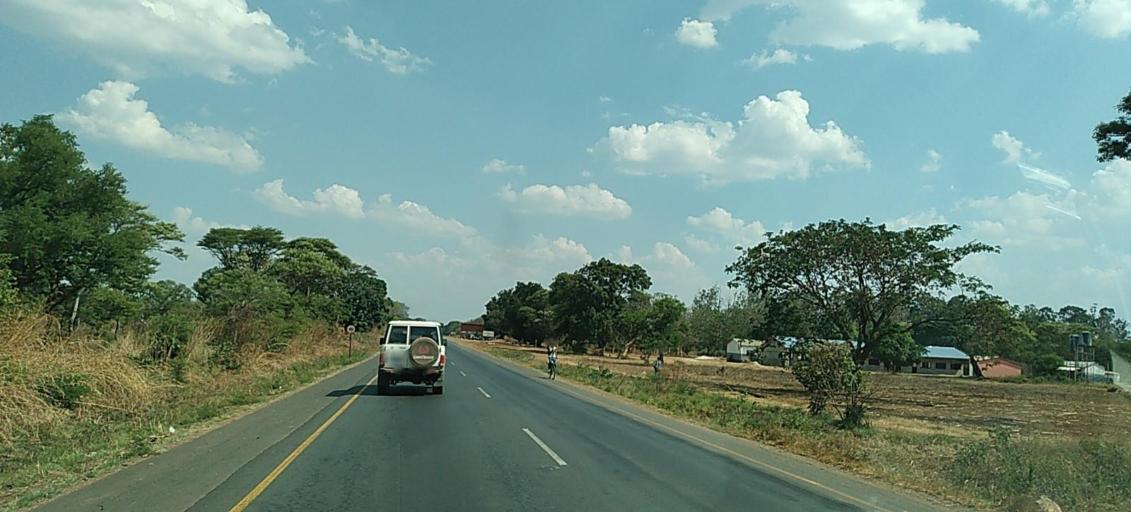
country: ZM
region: Central
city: Chibombo
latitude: -14.8775
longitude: 28.0596
